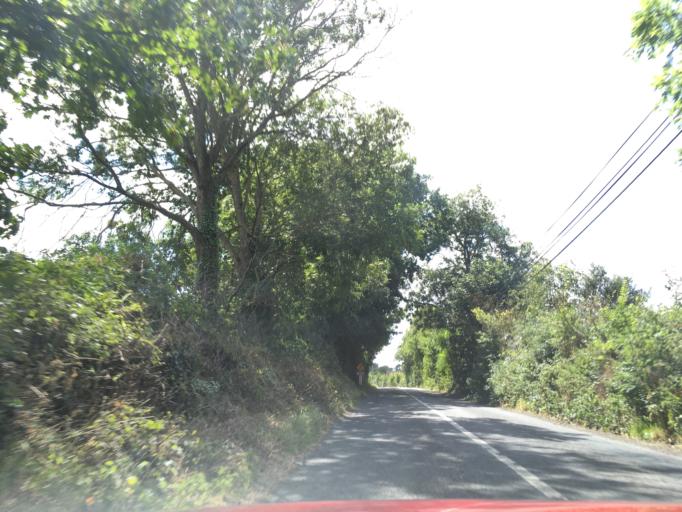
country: IE
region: Munster
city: Cahir
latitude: 52.3384
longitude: -7.9627
